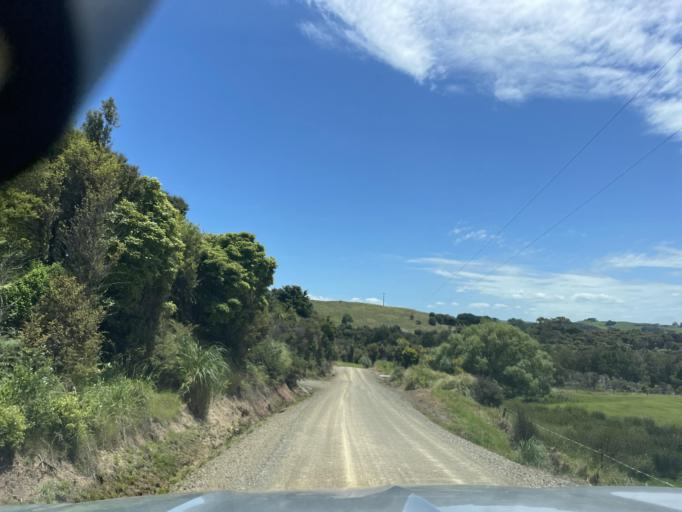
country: NZ
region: Auckland
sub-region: Auckland
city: Wellsford
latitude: -36.2179
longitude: 174.3573
